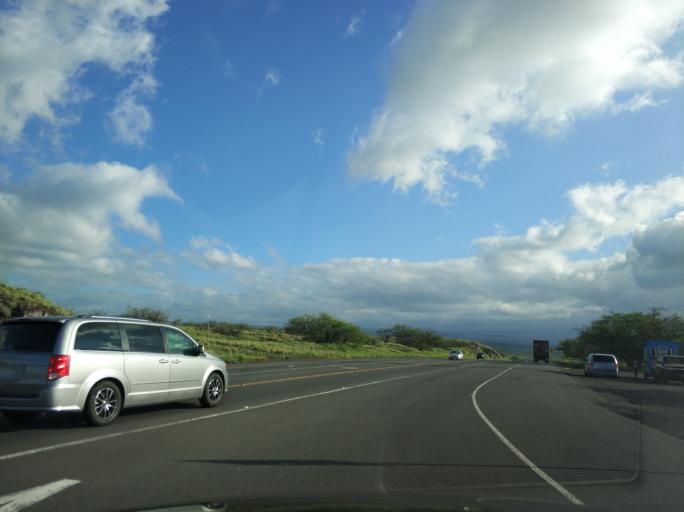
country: US
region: Hawaii
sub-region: Hawaii County
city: Waikoloa Village
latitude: 19.9742
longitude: -155.8206
